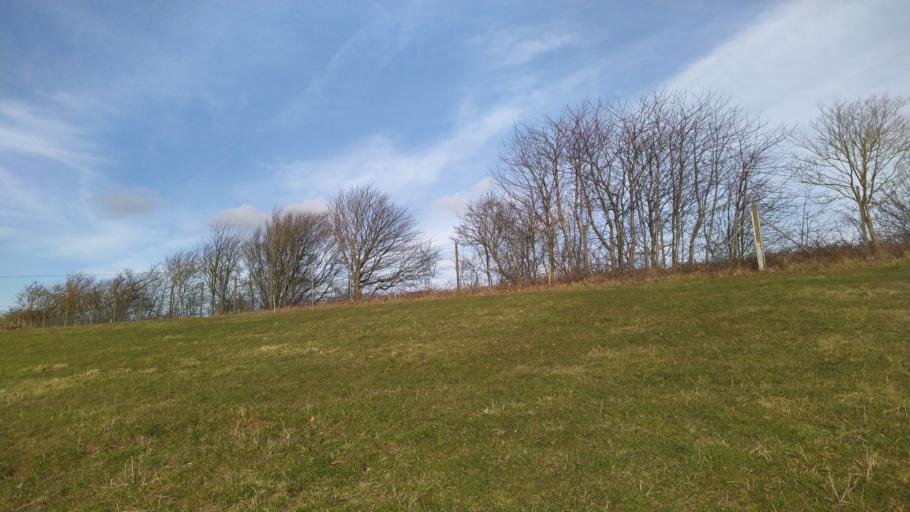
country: DK
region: South Denmark
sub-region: Fredericia Kommune
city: Taulov
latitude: 55.5138
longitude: 9.6078
